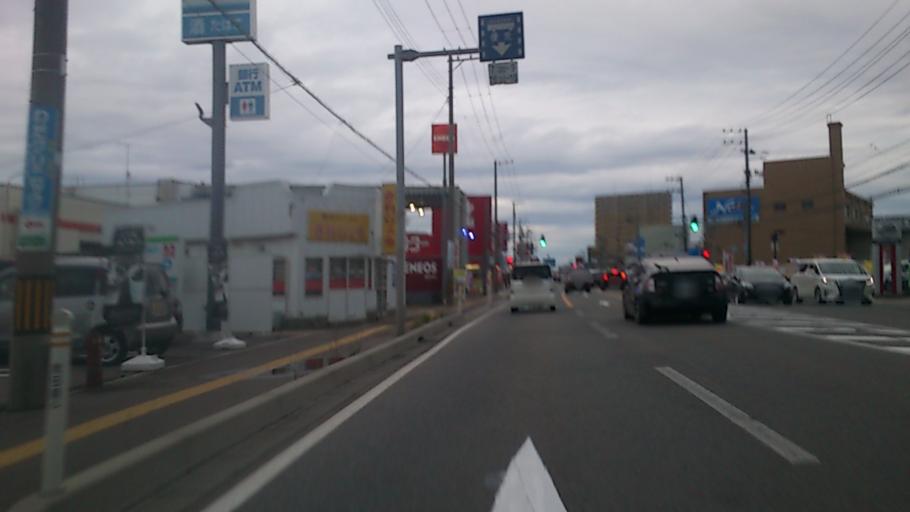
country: JP
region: Akita
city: Akita Shi
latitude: 39.7395
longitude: 140.0956
